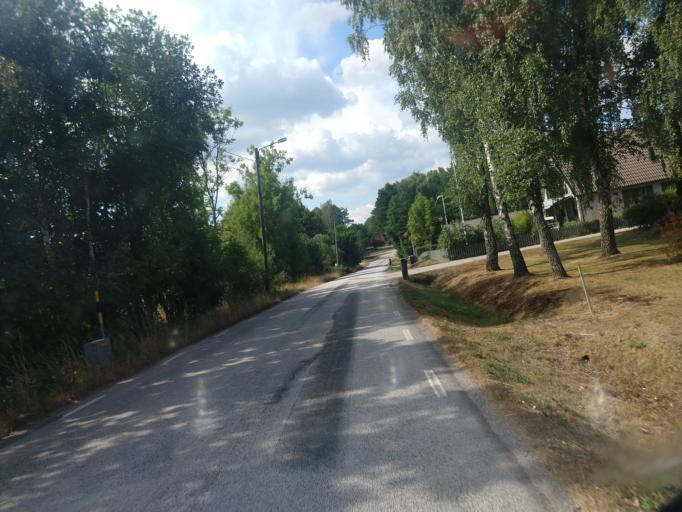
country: SE
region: Blekinge
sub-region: Karlskrona Kommun
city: Rodeby
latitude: 56.2425
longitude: 15.5609
